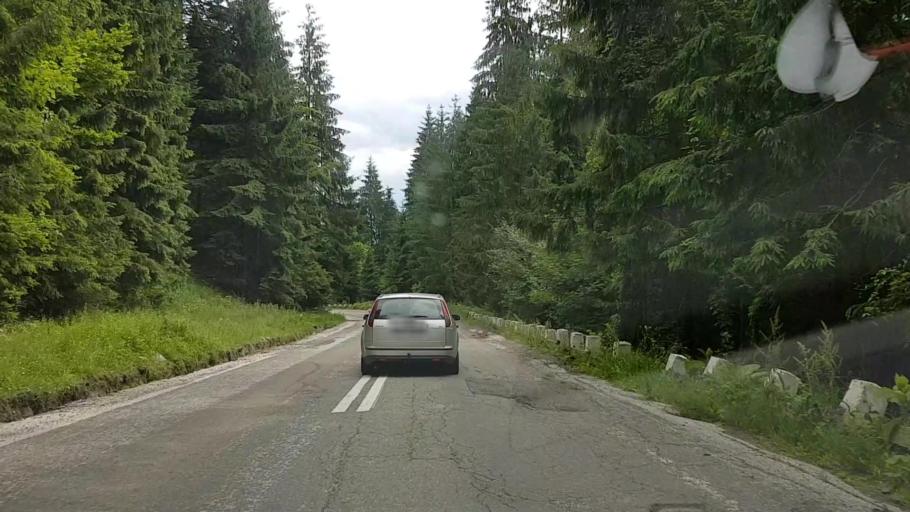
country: RO
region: Neamt
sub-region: Comuna Bicaz
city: Dodeni
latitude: 46.9682
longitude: 26.1163
